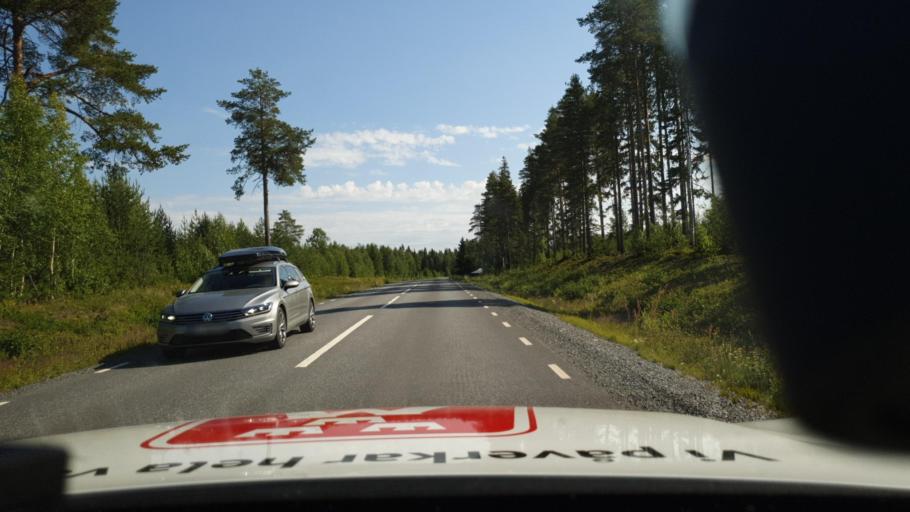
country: SE
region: Norrbotten
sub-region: Lulea Kommun
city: Gammelstad
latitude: 65.7879
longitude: 22.1095
